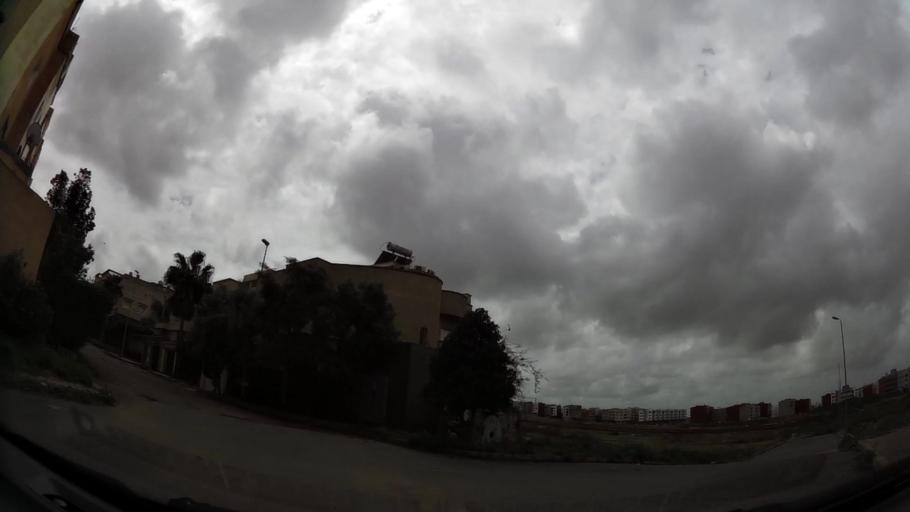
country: MA
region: Grand Casablanca
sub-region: Casablanca
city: Casablanca
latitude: 33.5294
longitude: -7.5970
